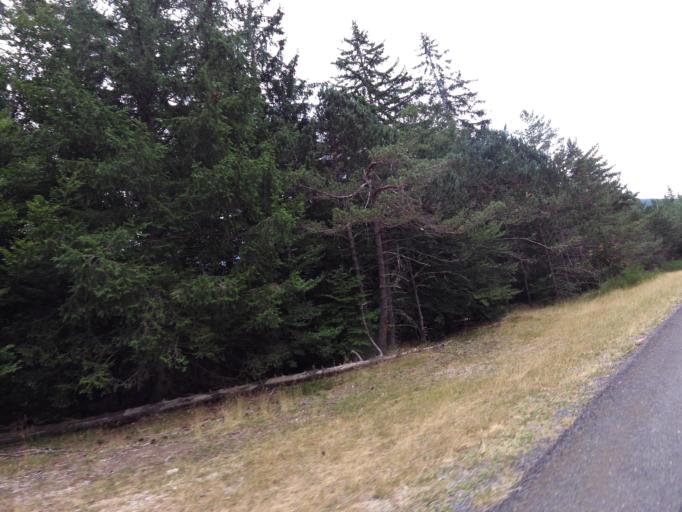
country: FR
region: Languedoc-Roussillon
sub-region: Departement du Gard
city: Valleraugue
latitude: 44.0841
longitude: 3.5630
